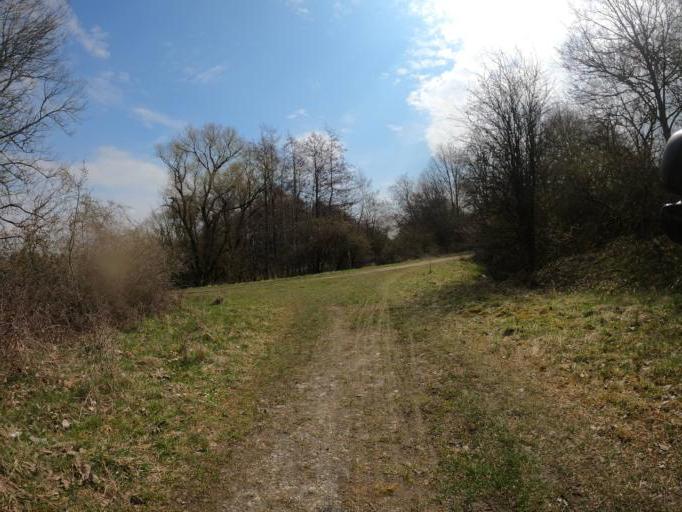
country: DE
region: North Rhine-Westphalia
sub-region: Regierungsbezirk Koln
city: Schleiden
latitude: 50.5785
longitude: 6.4265
